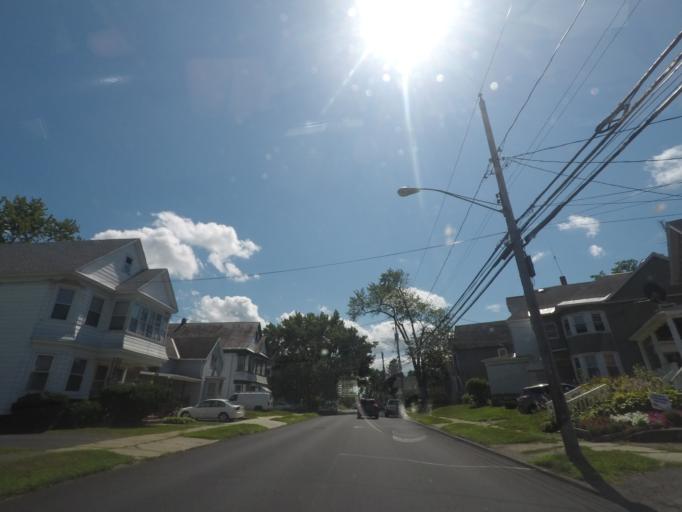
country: US
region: New York
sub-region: Schenectady County
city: Rotterdam
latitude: 42.7955
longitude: -73.9630
